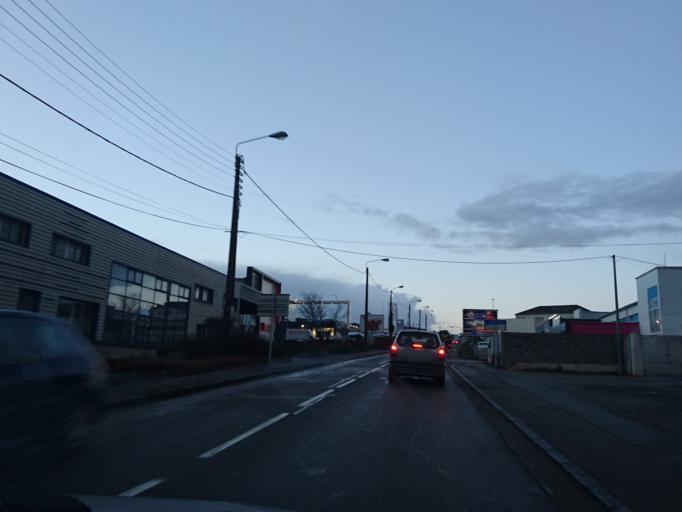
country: FR
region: Brittany
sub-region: Departement du Finistere
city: Brest
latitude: 48.4146
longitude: -4.4611
